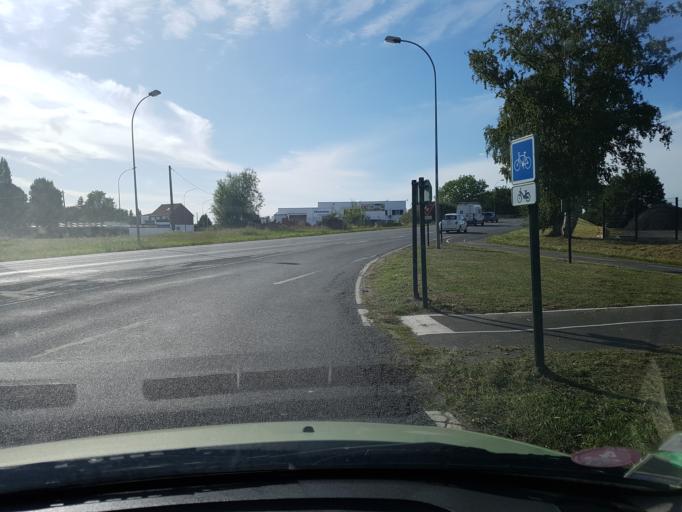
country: FR
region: Nord-Pas-de-Calais
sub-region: Departement du Pas-de-Calais
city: Annezin
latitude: 50.5318
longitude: 2.6101
